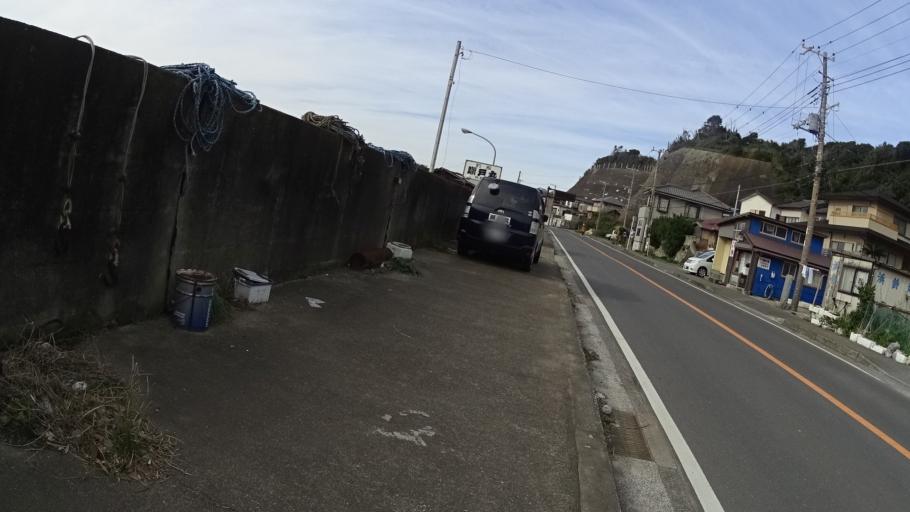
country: JP
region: Kanagawa
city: Miura
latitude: 35.1450
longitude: 139.6690
